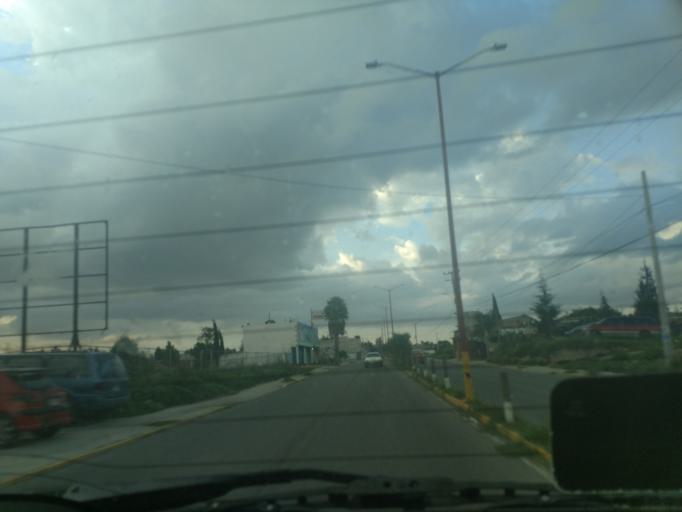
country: MX
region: Morelos
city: Coyotepec
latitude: 19.7657
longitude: -99.2013
